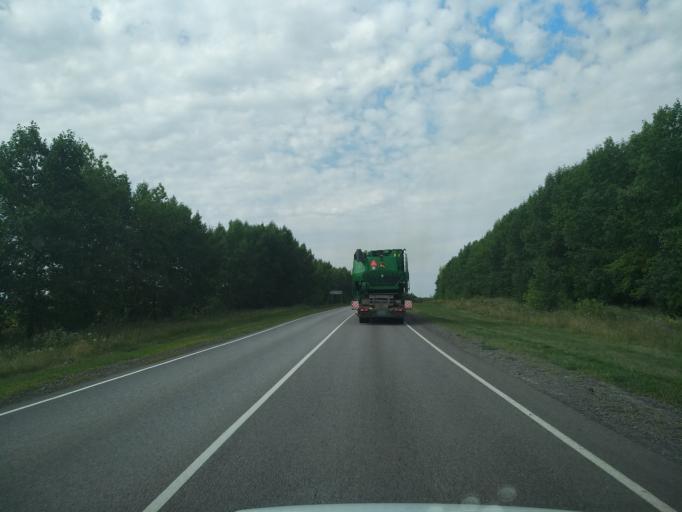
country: RU
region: Voronezj
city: Pereleshinskiy
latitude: 51.8777
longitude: 40.4138
